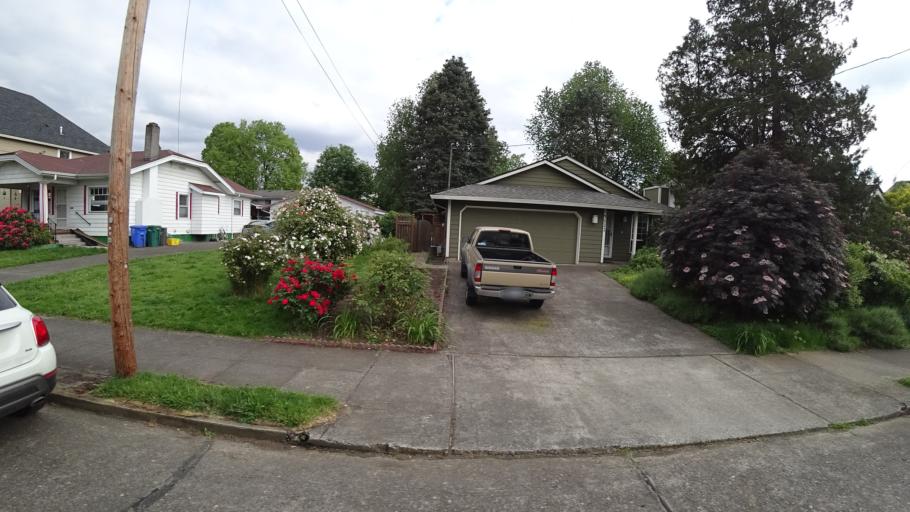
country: US
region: Oregon
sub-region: Multnomah County
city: Portland
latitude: 45.5179
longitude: -122.6171
